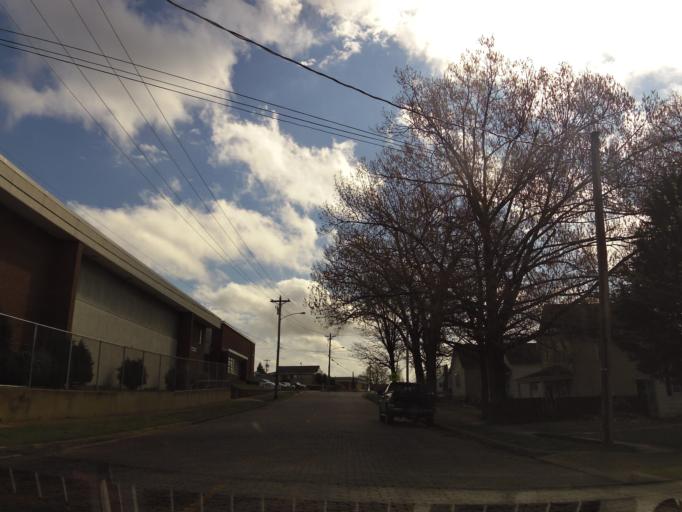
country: US
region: Missouri
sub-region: Butler County
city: Poplar Bluff
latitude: 36.7574
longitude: -90.4012
